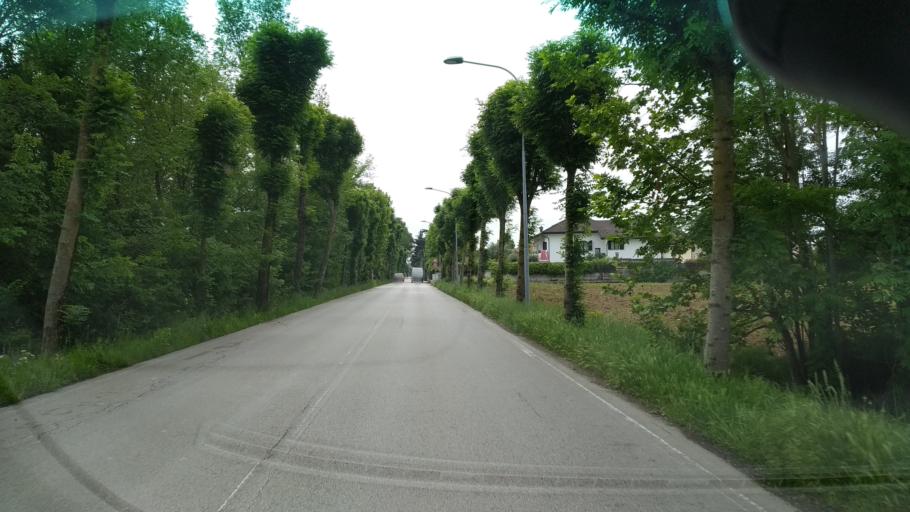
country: IT
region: Veneto
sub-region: Provincia di Vicenza
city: Caldogno-Rettorgole-Cresole
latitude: 45.5970
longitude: 11.5193
